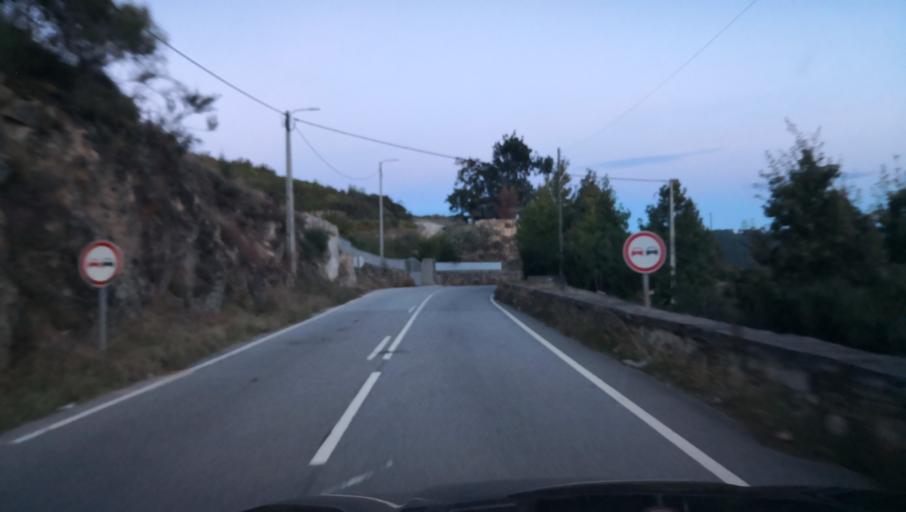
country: PT
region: Vila Real
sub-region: Vila Real
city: Vila Real
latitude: 41.2737
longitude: -7.7722
